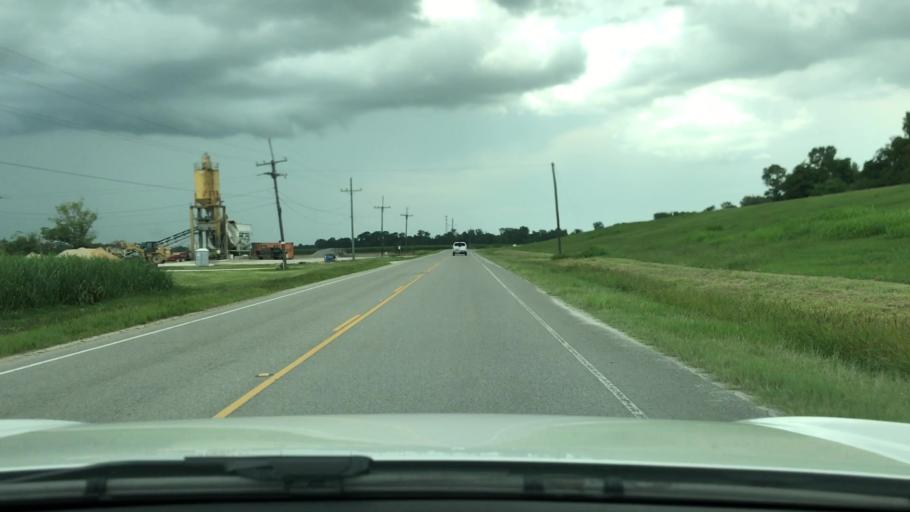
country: US
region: Louisiana
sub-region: Iberville Parish
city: Plaquemine
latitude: 30.2728
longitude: -91.1974
